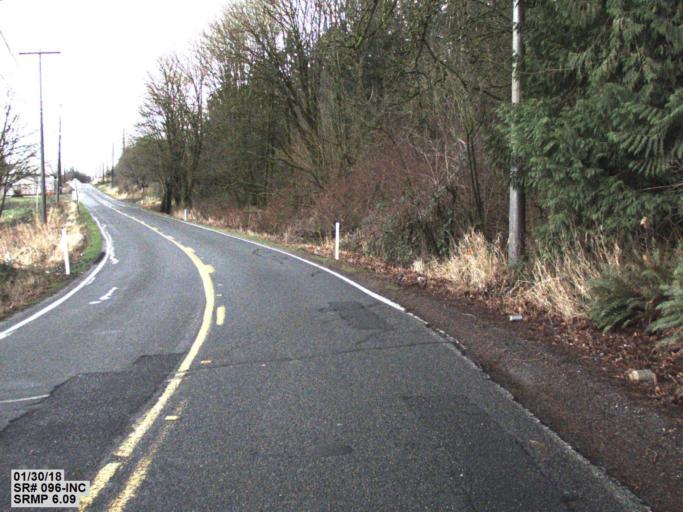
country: US
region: Washington
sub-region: Snohomish County
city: Silver Firs
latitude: 47.8800
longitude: -122.1235
